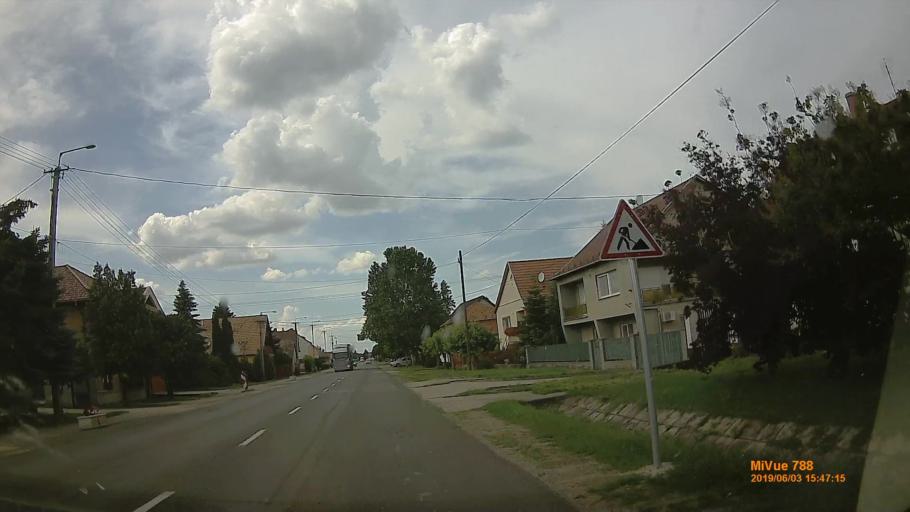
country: HU
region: Bacs-Kiskun
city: Akaszto
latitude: 46.6845
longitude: 19.2109
